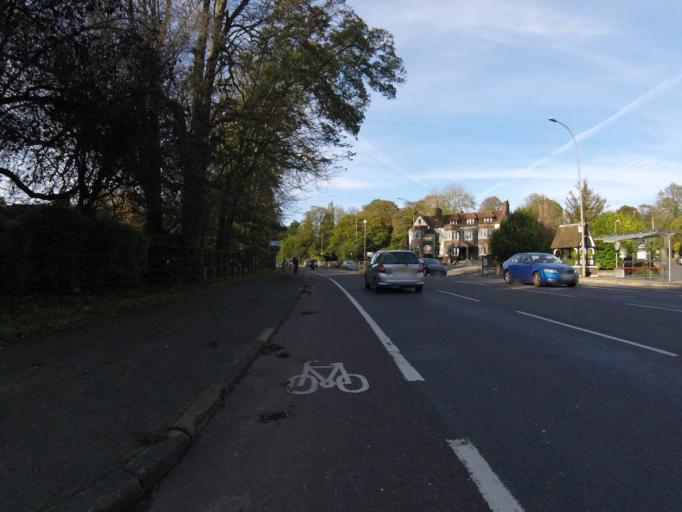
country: GB
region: England
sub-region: Brighton and Hove
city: Hove
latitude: 50.8648
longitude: -0.1524
